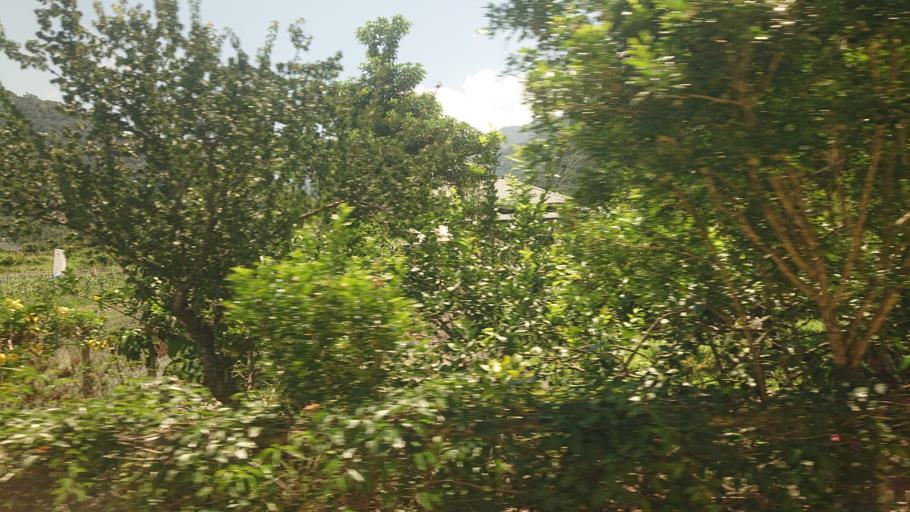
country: TW
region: Taiwan
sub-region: Nantou
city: Puli
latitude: 24.0644
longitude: 120.9531
